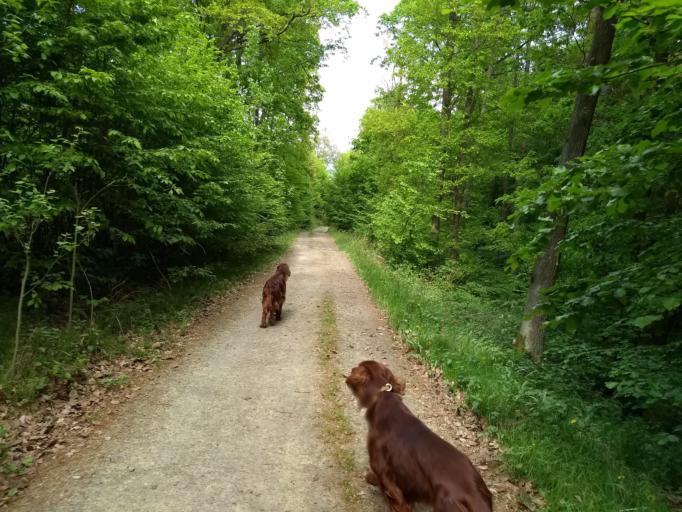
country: CZ
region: Central Bohemia
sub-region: Okres Beroun
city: Lodenice
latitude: 50.0444
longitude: 14.1581
